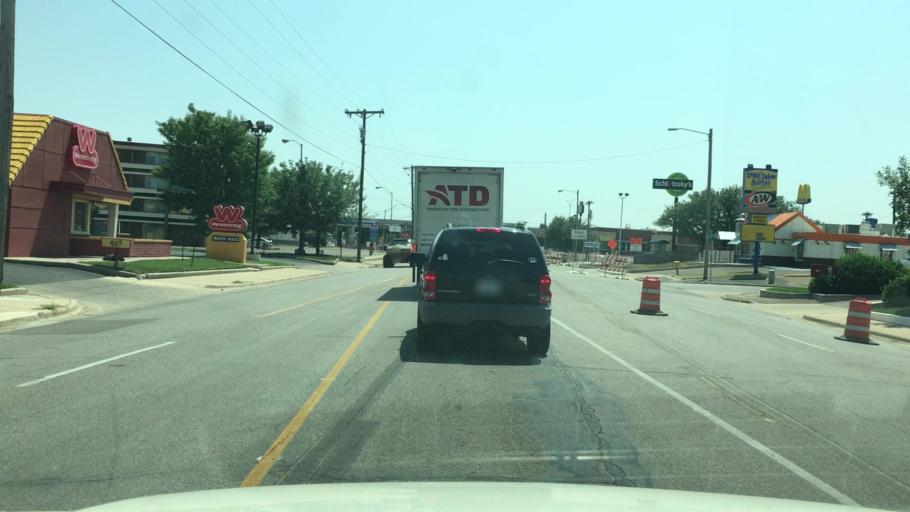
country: US
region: Texas
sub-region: Potter County
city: Amarillo
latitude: 35.1949
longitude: -101.8172
